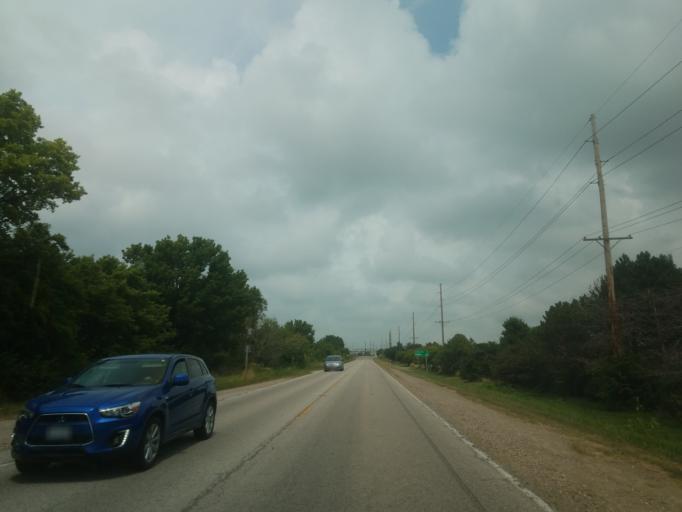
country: US
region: Illinois
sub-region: McLean County
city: Bloomington
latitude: 40.4910
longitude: -89.0175
